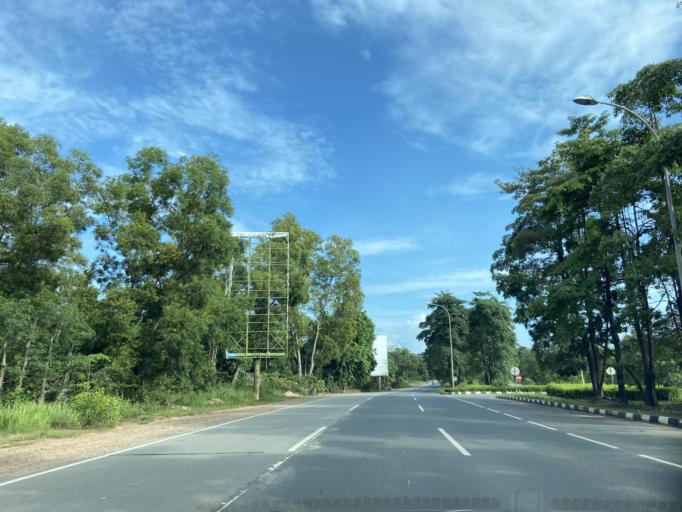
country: SG
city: Singapore
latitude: 1.1045
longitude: 104.0335
